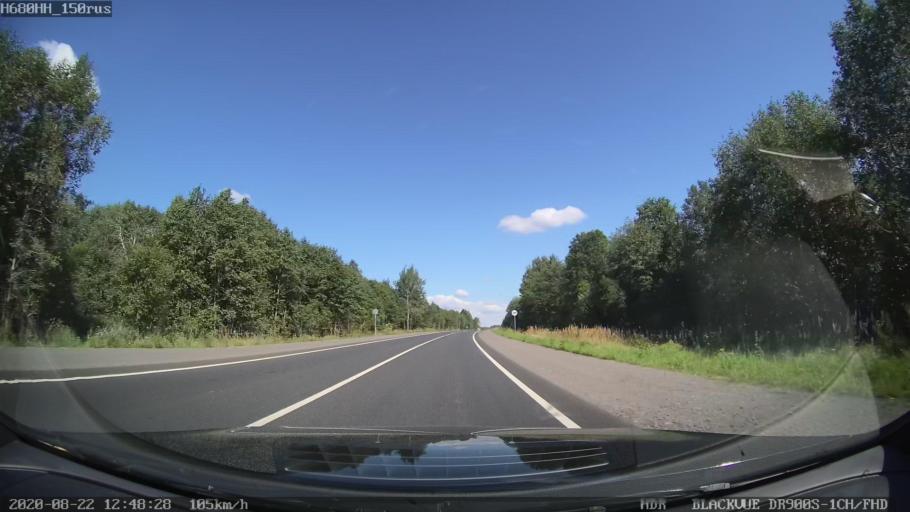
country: RU
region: Tverskaya
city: Rameshki
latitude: 57.4402
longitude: 36.1848
